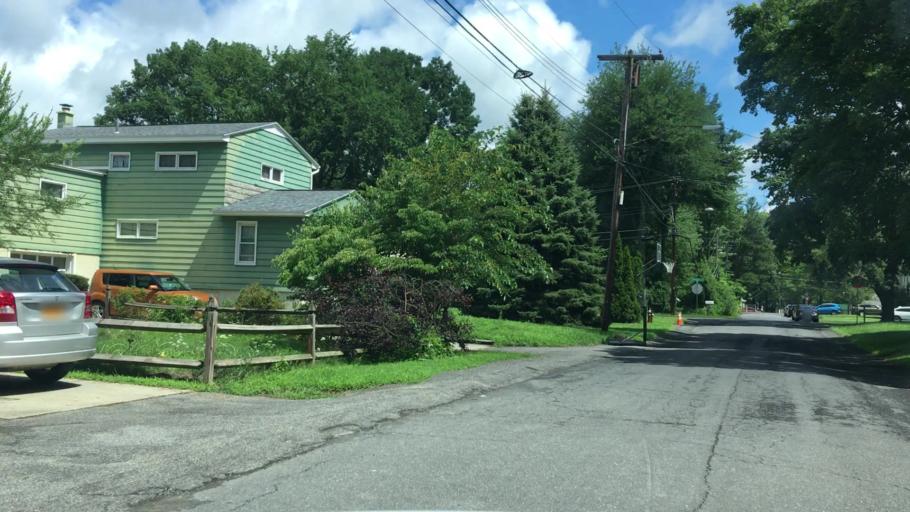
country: US
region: New York
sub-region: Schenectady County
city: Niskayuna
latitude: 42.7457
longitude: -73.8623
